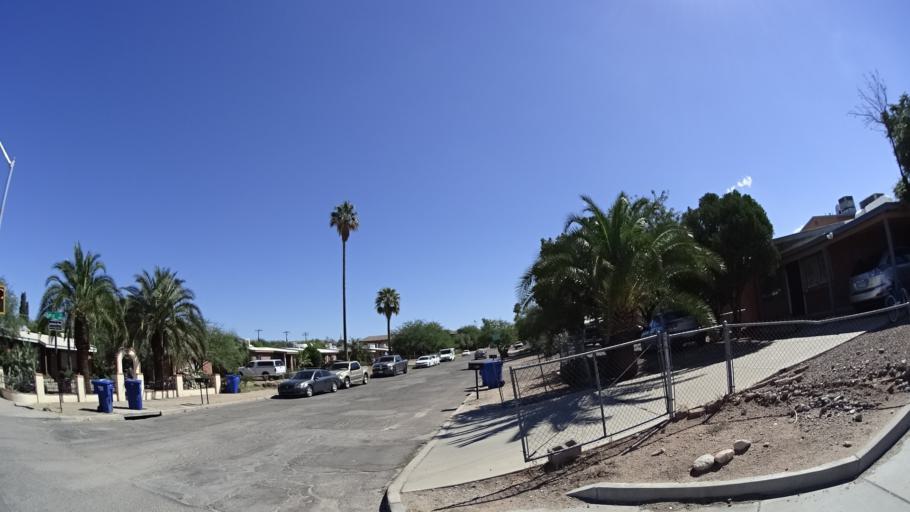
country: US
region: Arizona
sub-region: Pima County
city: Tucson
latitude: 32.2435
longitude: -110.9595
